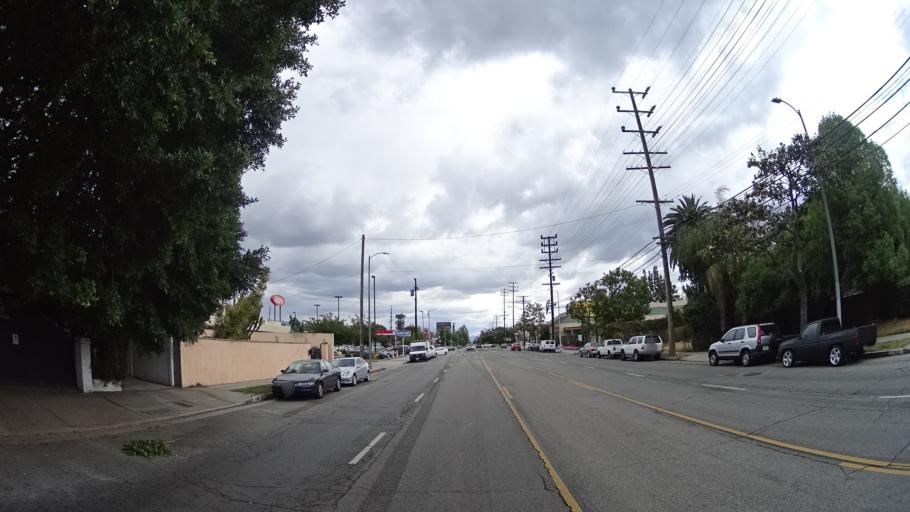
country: US
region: California
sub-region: Los Angeles County
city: Sherman Oaks
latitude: 34.1649
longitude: -118.4153
